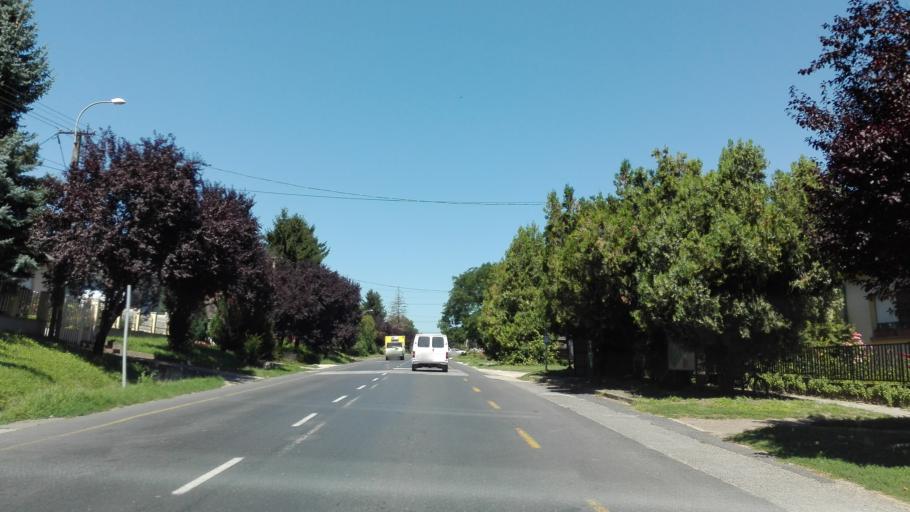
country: HU
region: Fejer
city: Mezoszilas
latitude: 46.8183
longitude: 18.4790
